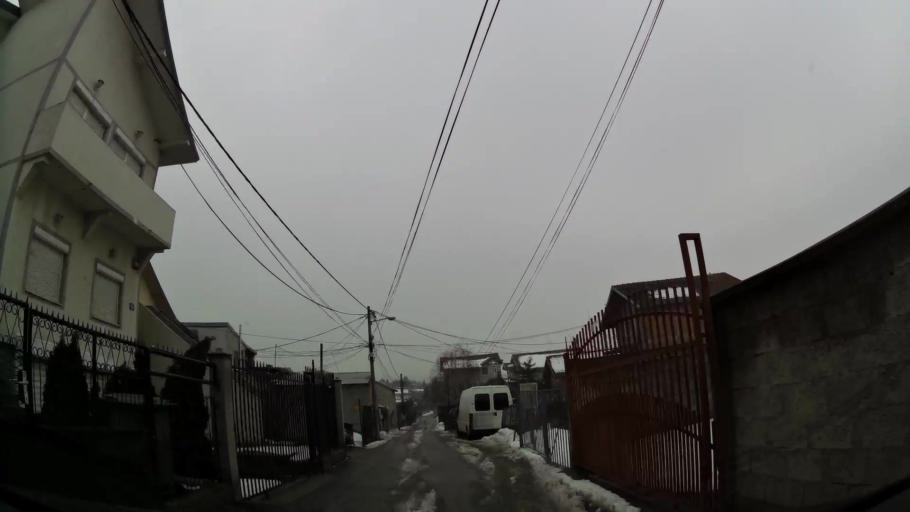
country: RS
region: Central Serbia
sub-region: Belgrade
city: Zvezdara
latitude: 44.7765
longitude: 20.5186
